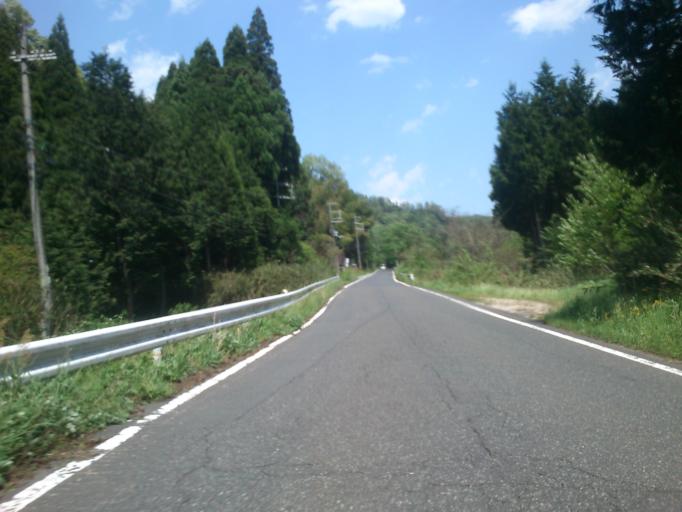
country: JP
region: Kyoto
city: Miyazu
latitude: 35.6867
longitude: 135.1129
